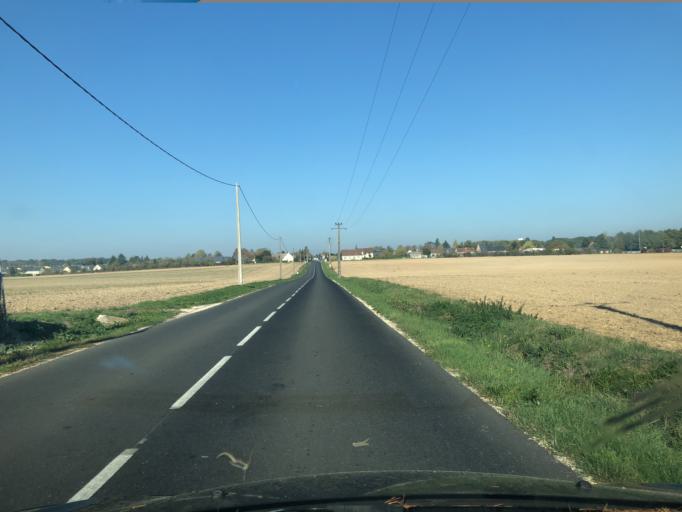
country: FR
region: Centre
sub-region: Departement d'Indre-et-Loire
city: Rouziers-de-Touraine
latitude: 47.5096
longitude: 0.6503
